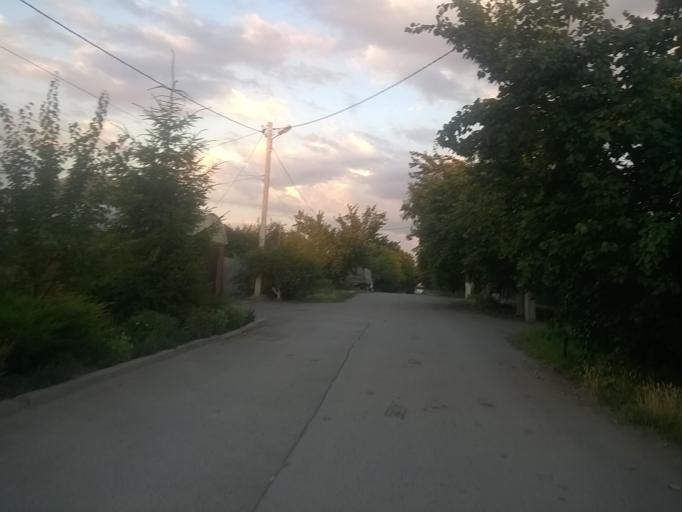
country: RU
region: Rostov
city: Donetsk
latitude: 48.3352
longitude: 39.9537
